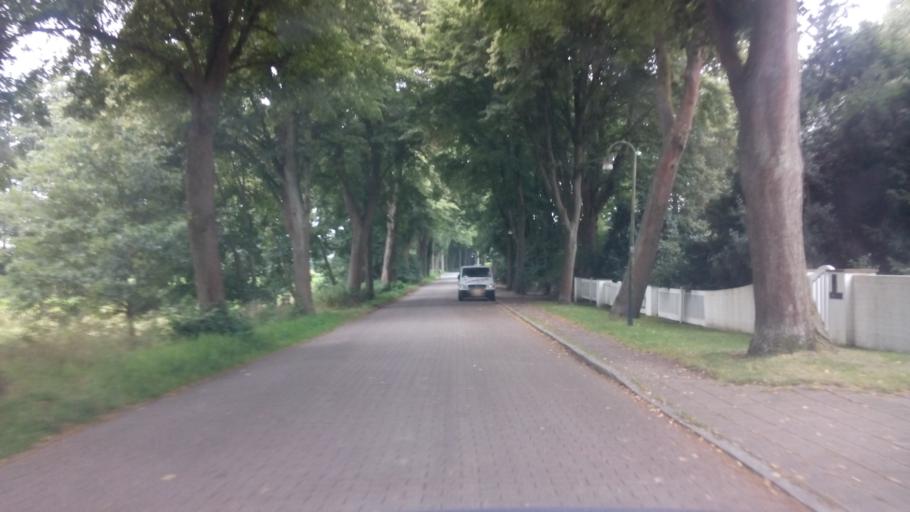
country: DE
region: Lower Saxony
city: Lilienthal
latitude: 53.1212
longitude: 8.8837
